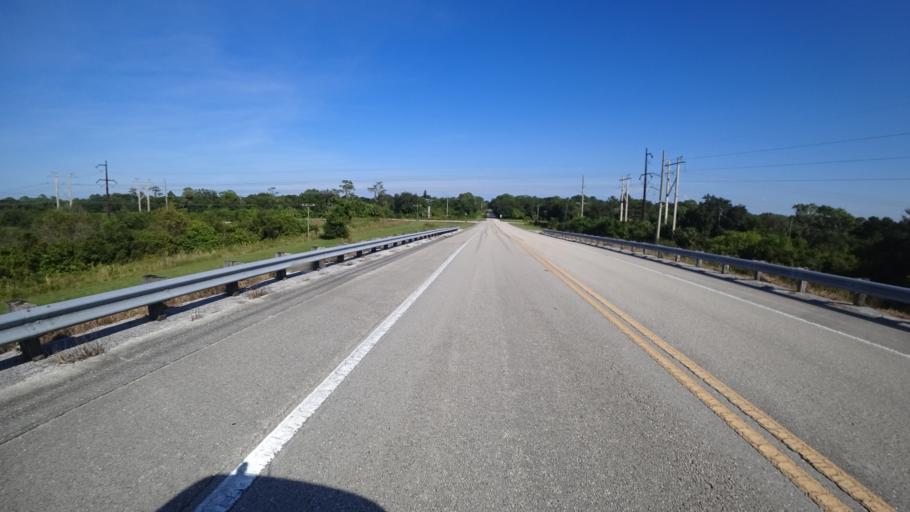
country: US
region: Florida
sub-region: Sarasota County
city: Desoto Lakes
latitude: 27.4178
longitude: -82.4556
